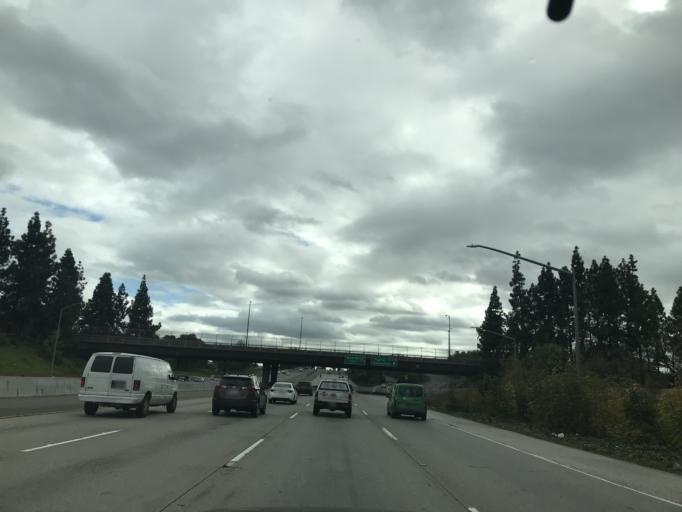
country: US
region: California
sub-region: Santa Clara County
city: Alum Rock
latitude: 37.3607
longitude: -121.8420
